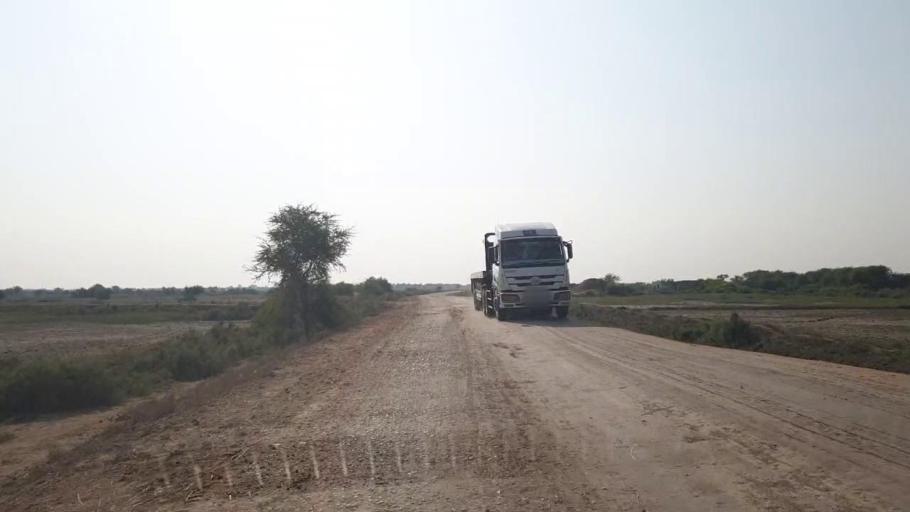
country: PK
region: Sindh
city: Matli
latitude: 24.9345
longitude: 68.6682
